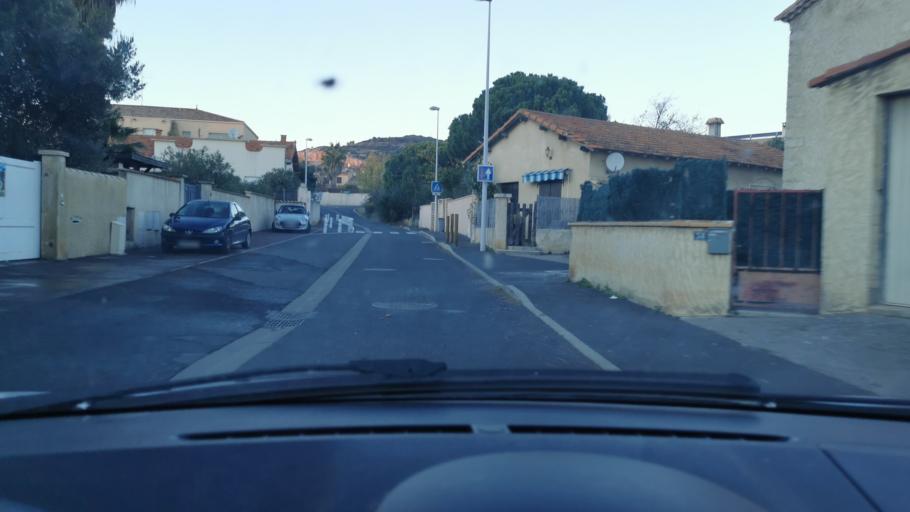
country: FR
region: Languedoc-Roussillon
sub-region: Departement de l'Herault
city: Frontignan
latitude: 43.4541
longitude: 3.7539
